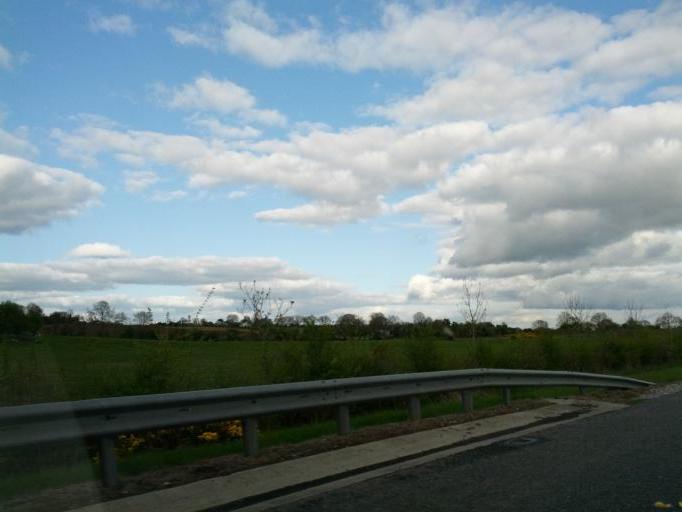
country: IE
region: Leinster
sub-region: Uibh Fhaili
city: Clara
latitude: 53.3809
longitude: -7.5689
